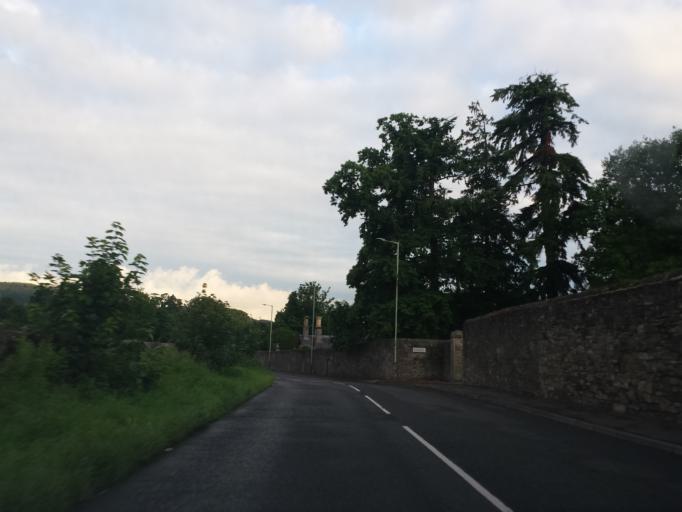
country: GB
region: Scotland
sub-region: Perth and Kinross
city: Perth
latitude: 56.4083
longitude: -3.4281
